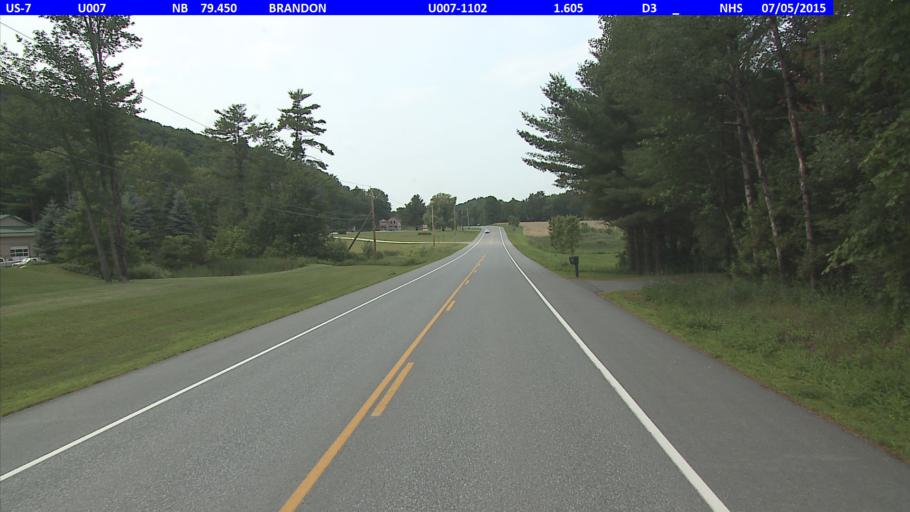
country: US
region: Vermont
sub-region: Rutland County
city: Brandon
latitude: 43.7778
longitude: -73.0563
